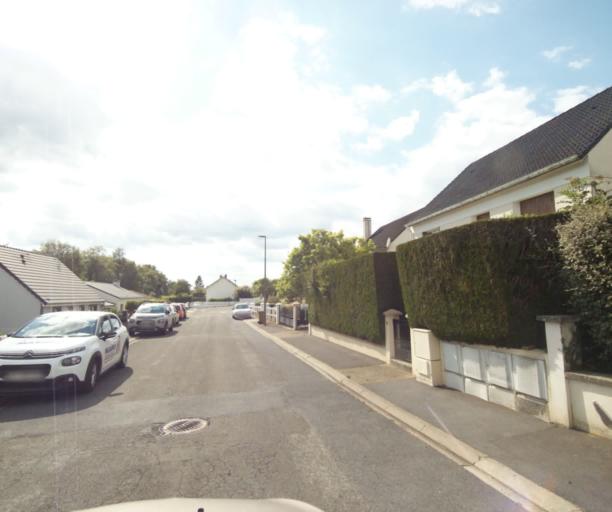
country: FR
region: Champagne-Ardenne
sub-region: Departement des Ardennes
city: Montcy-Notre-Dame
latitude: 49.7594
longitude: 4.7458
